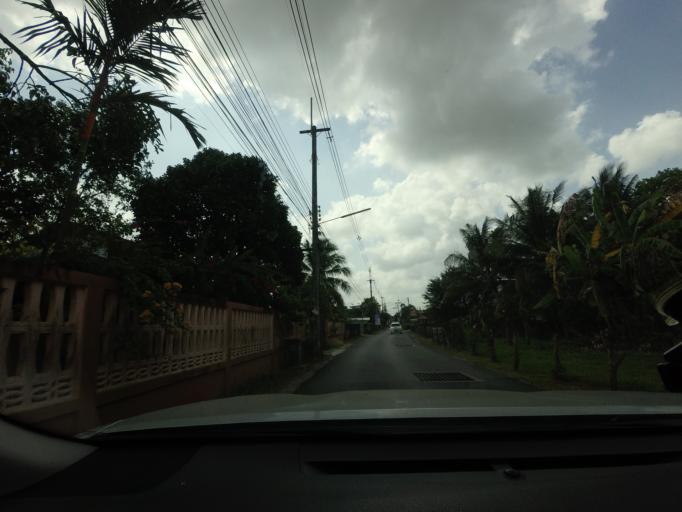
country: TH
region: Nakhon Si Thammarat
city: Nakhon Si Thammarat
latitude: 8.4363
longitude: 99.9309
